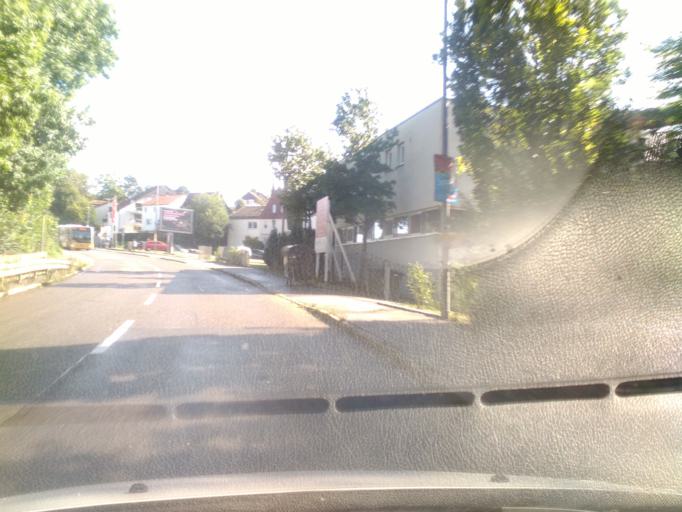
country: DE
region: Baden-Wuerttemberg
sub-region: Regierungsbezirk Stuttgart
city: Leinfelden-Echterdingen
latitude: 48.7042
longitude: 9.2044
